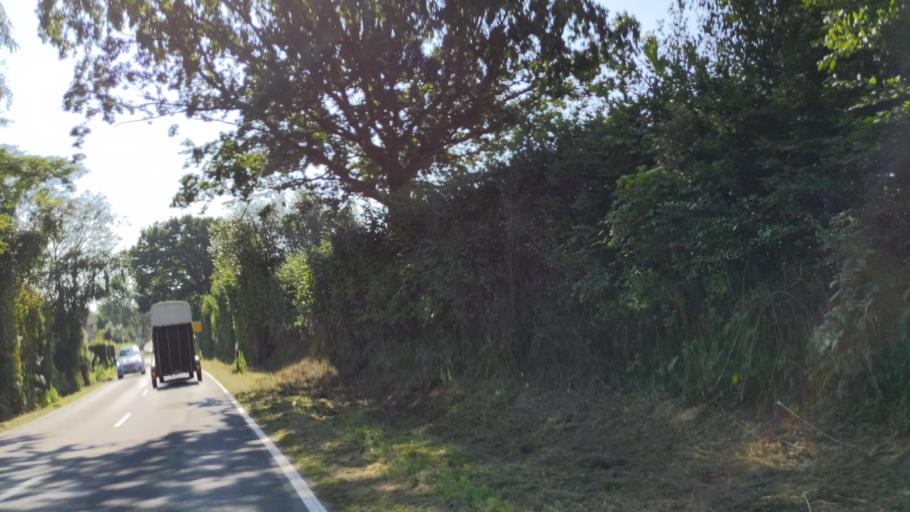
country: DE
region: Schleswig-Holstein
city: Gross Schenkenberg
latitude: 53.8019
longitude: 10.6014
